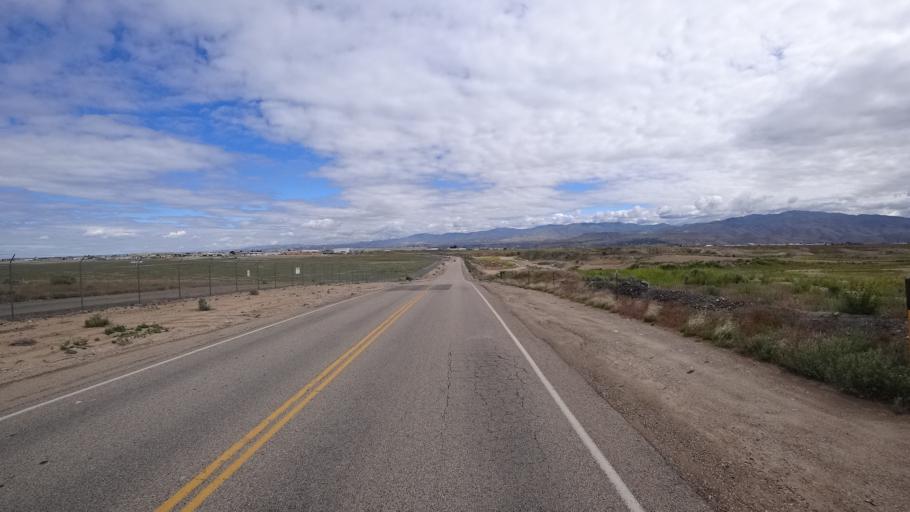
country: US
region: Idaho
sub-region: Ada County
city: Boise
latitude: 43.5486
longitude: -116.1882
